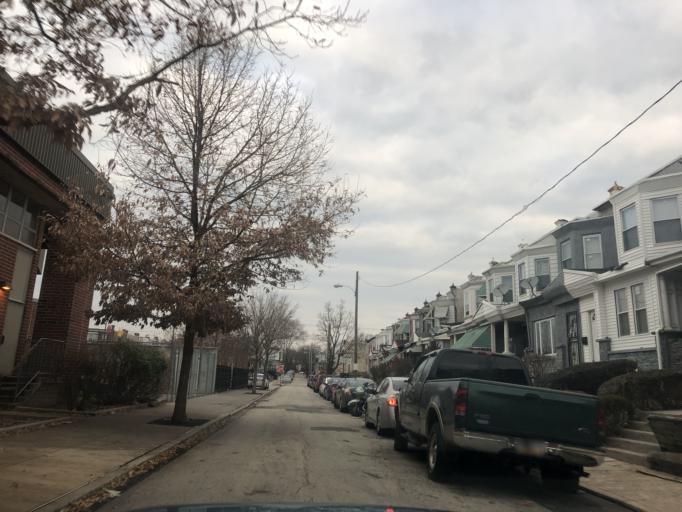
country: US
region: Pennsylvania
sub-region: Delaware County
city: Millbourne
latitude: 39.9738
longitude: -75.2356
